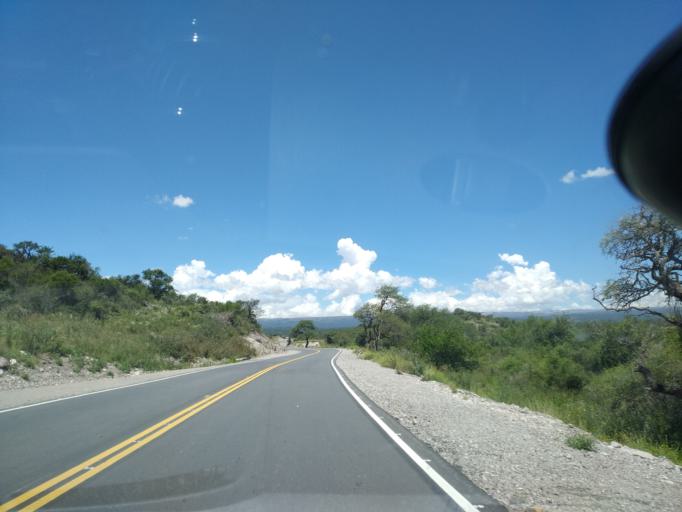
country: AR
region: Cordoba
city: Salsacate
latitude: -31.3458
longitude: -65.0945
